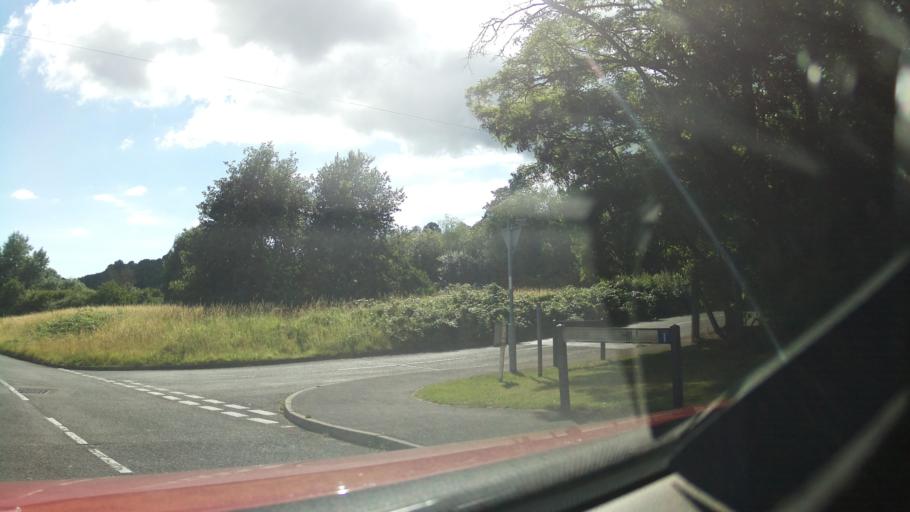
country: GB
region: England
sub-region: South Gloucestershire
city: Stoke Gifford
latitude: 51.4827
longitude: -2.5581
